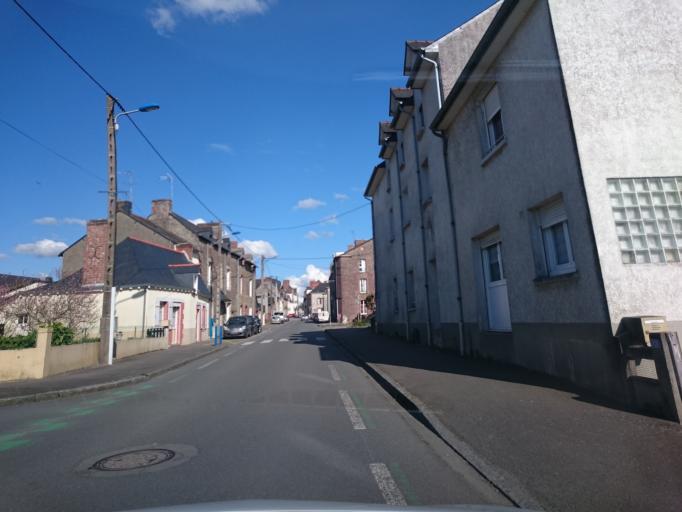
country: FR
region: Brittany
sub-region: Departement d'Ille-et-Vilaine
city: Janze
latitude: 47.9592
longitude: -1.5025
